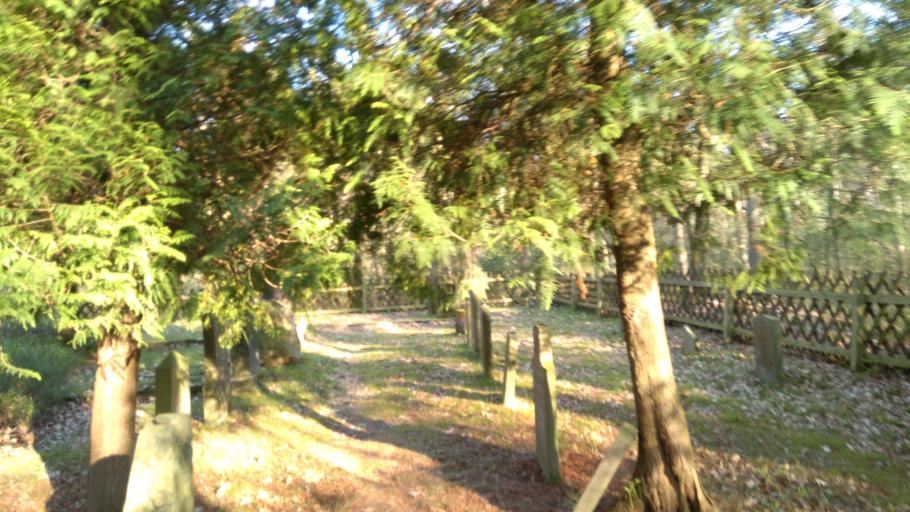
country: DE
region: Lower Saxony
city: Buxtehude
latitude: 53.4718
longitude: 9.6593
